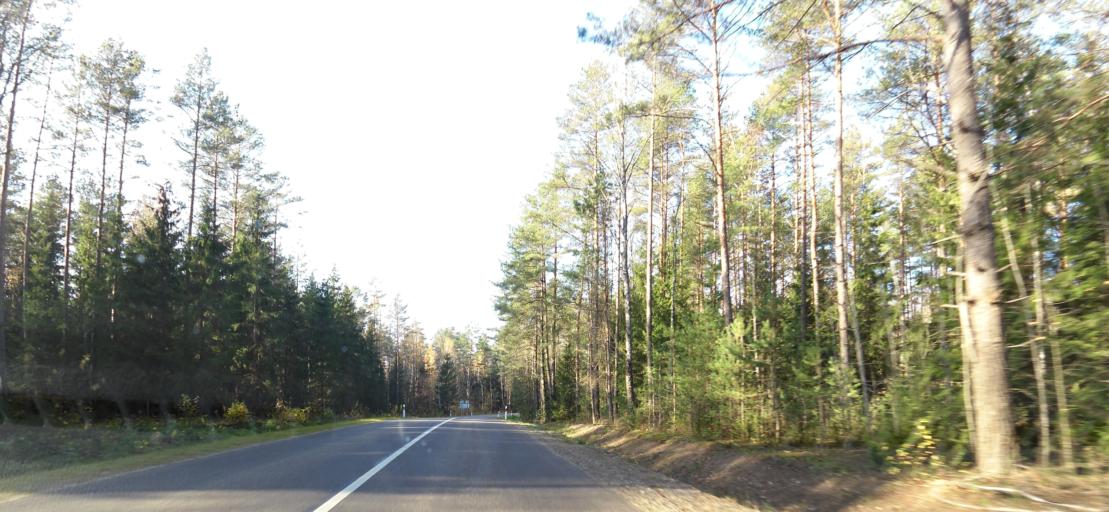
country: LT
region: Vilnius County
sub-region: Trakai
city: Rudiskes
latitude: 54.5092
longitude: 24.8848
